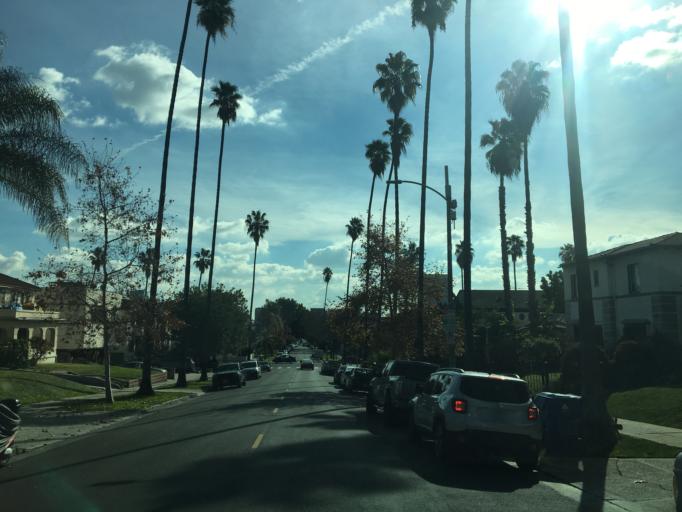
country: US
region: California
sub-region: Los Angeles County
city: Silver Lake
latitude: 34.0737
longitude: -118.2955
